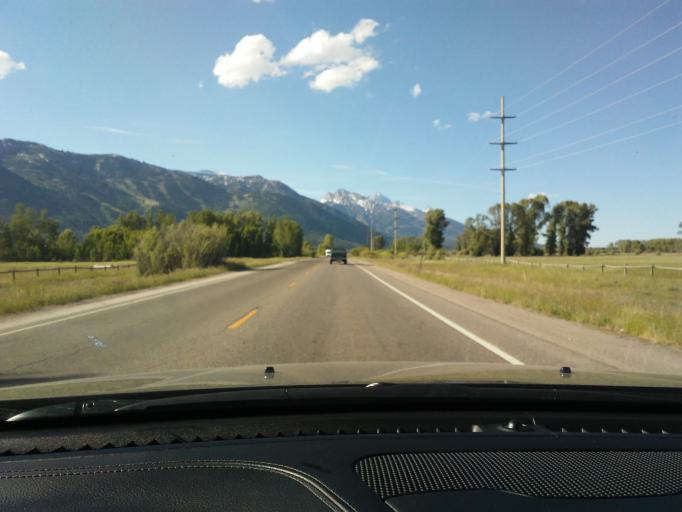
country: US
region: Wyoming
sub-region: Teton County
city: Moose Wilson Road
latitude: 43.5544
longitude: -110.8223
